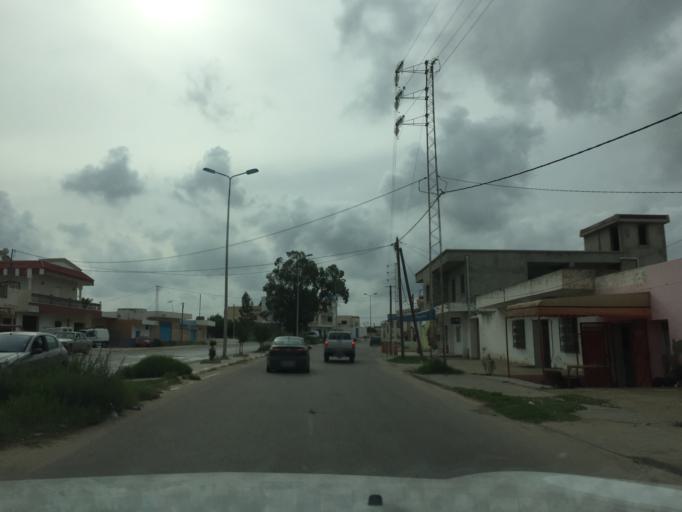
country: TN
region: Susah
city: Masakin
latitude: 35.6667
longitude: 10.5812
